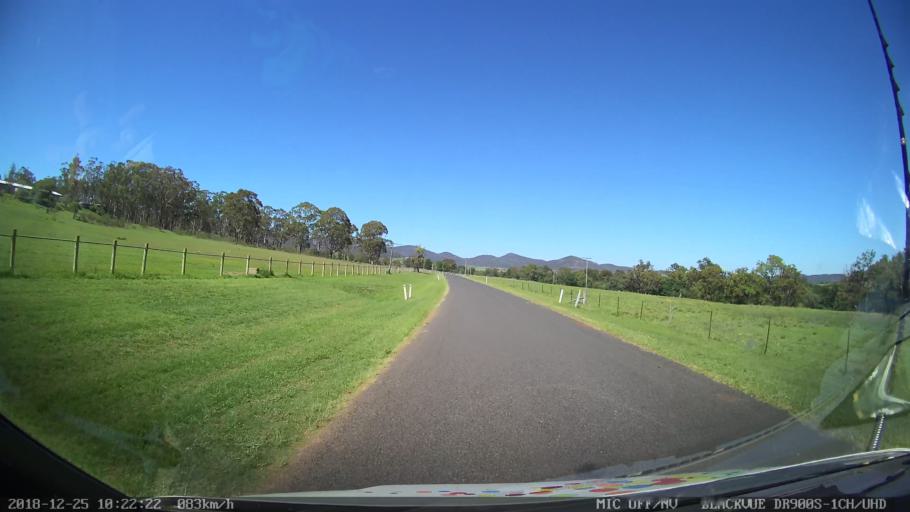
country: AU
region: New South Wales
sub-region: Muswellbrook
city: Denman
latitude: -32.3759
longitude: 150.5332
